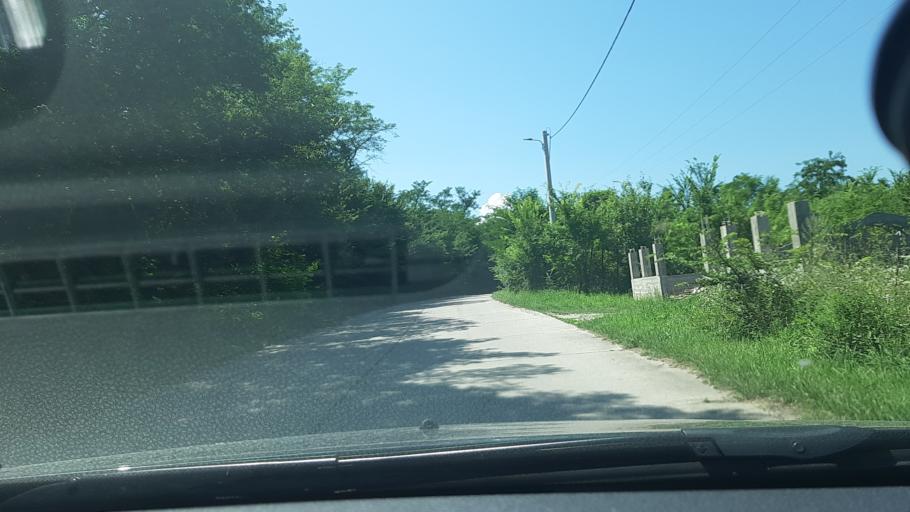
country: RO
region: Hunedoara
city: Bucium-Orlea
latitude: 45.5874
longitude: 22.9634
